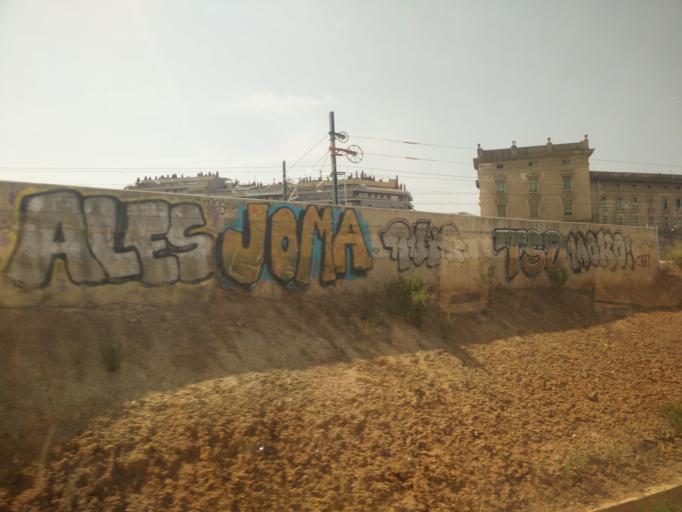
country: ES
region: Catalonia
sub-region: Provincia de Barcelona
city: Sant Marti
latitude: 41.4180
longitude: 2.1927
